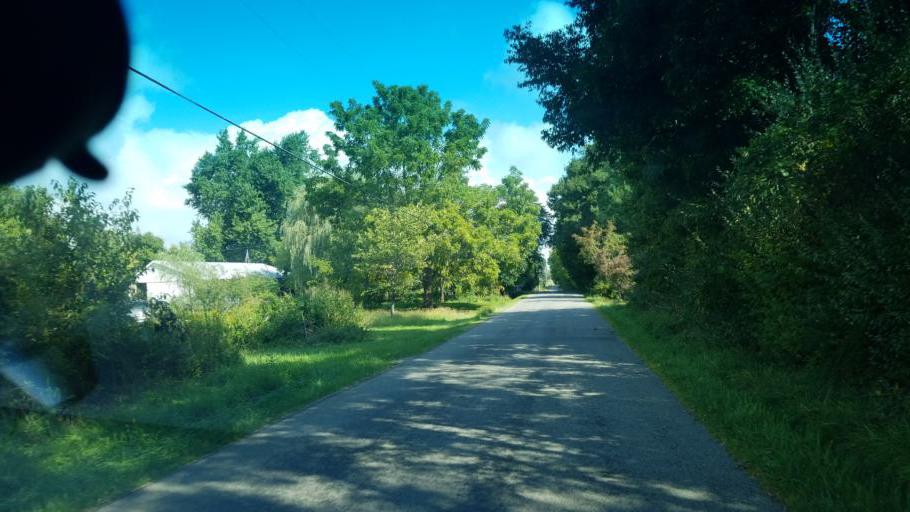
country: US
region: Ohio
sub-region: Licking County
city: Granville
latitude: 40.1658
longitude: -82.5637
